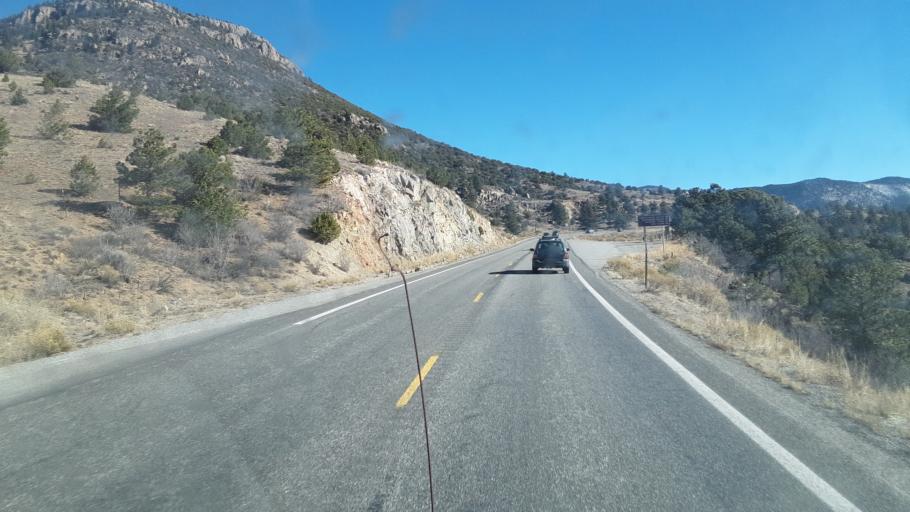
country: US
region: Colorado
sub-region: Chaffee County
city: Buena Vista
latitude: 38.8412
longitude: -106.0122
